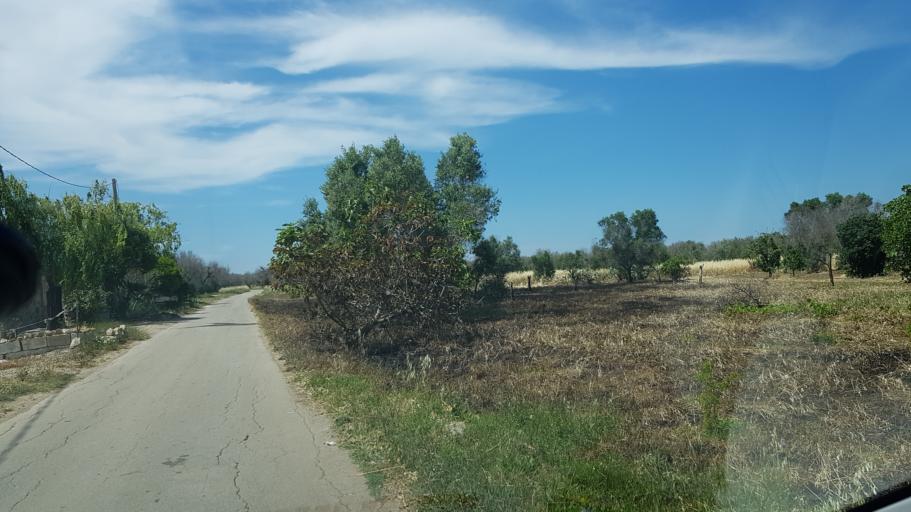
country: IT
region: Apulia
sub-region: Provincia di Brindisi
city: San Pietro Vernotico
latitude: 40.5242
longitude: 18.0102
